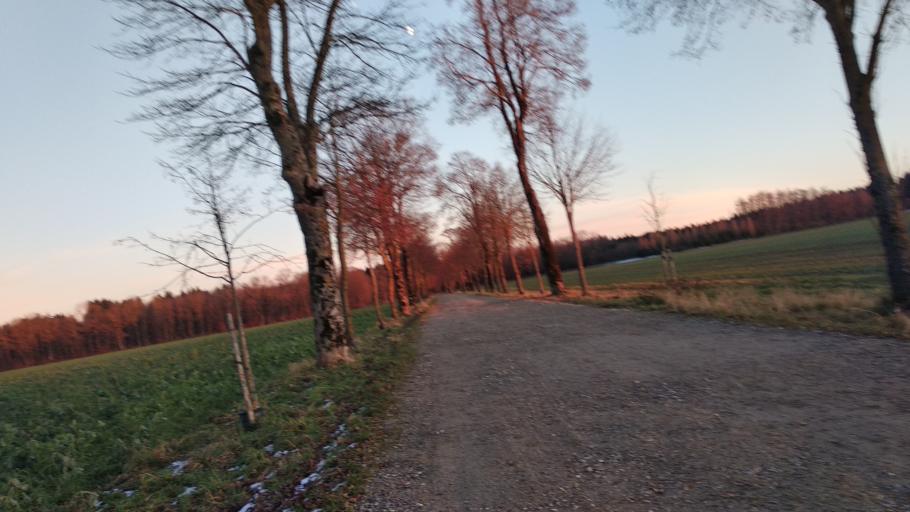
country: DE
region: Bavaria
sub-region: Upper Bavaria
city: Vaterstetten
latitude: 48.0705
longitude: 11.7808
